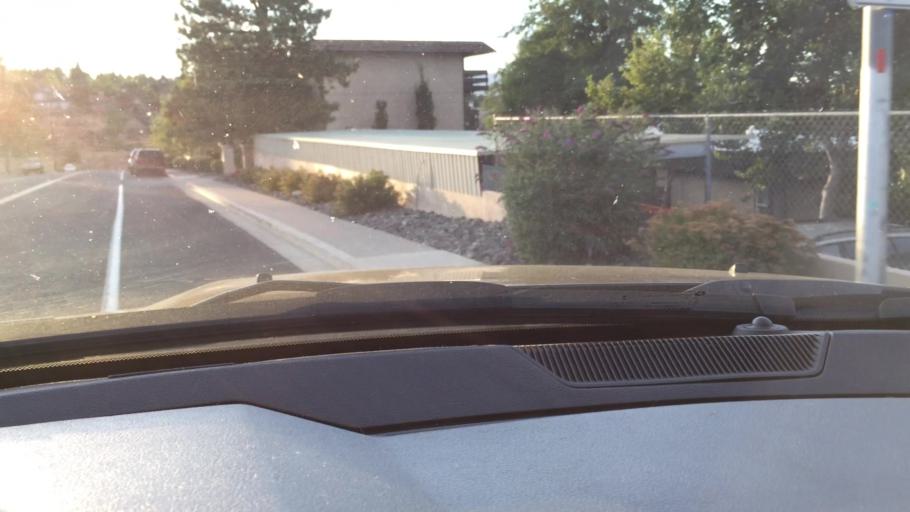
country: US
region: Nevada
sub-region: Washoe County
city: Reno
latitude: 39.4827
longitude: -119.8366
